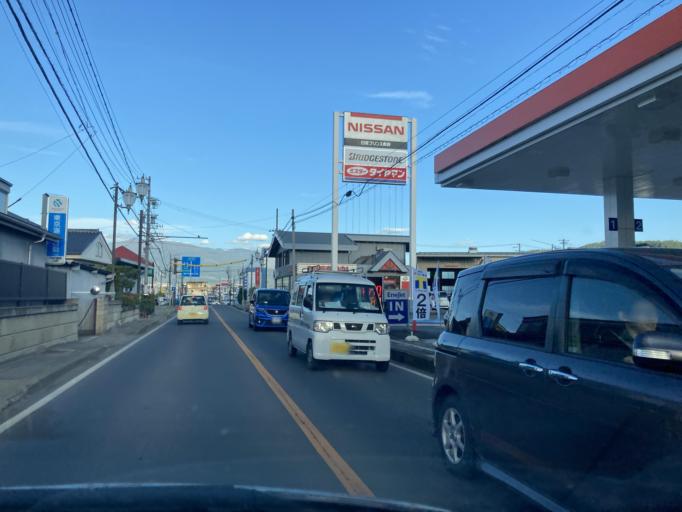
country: JP
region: Nagano
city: Ueda
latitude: 36.3888
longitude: 138.2071
